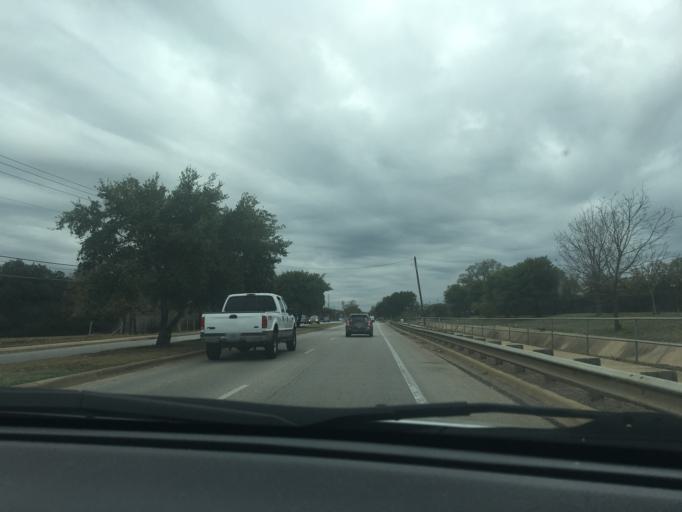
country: US
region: Texas
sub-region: Travis County
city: Shady Hollow
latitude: 30.2186
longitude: -97.8275
